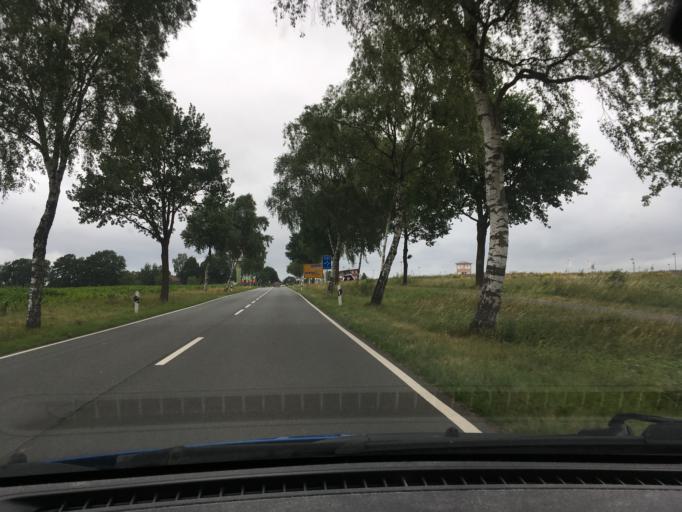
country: DE
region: Lower Saxony
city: Bispingen
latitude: 53.0970
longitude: 9.9822
